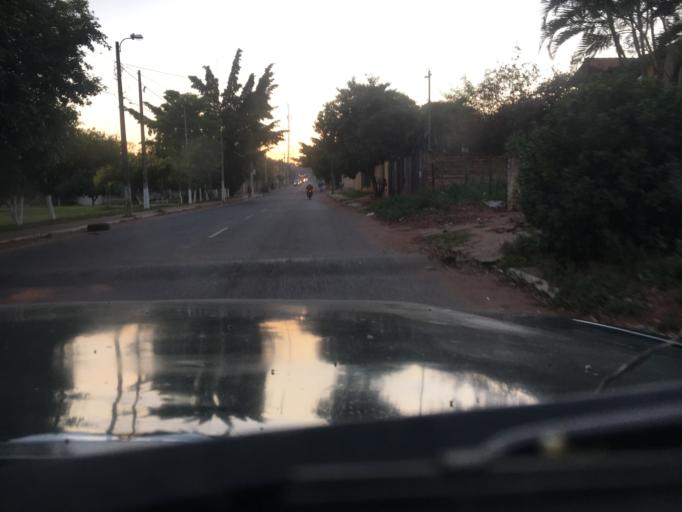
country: PY
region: Central
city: Villa Elisa
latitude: -25.3721
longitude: -57.5877
